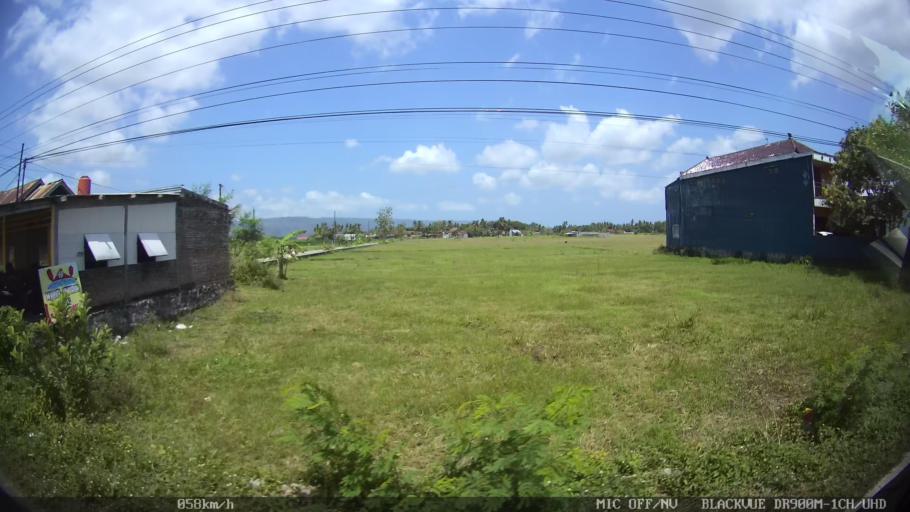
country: ID
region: Daerah Istimewa Yogyakarta
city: Sewon
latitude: -7.9112
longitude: 110.3584
